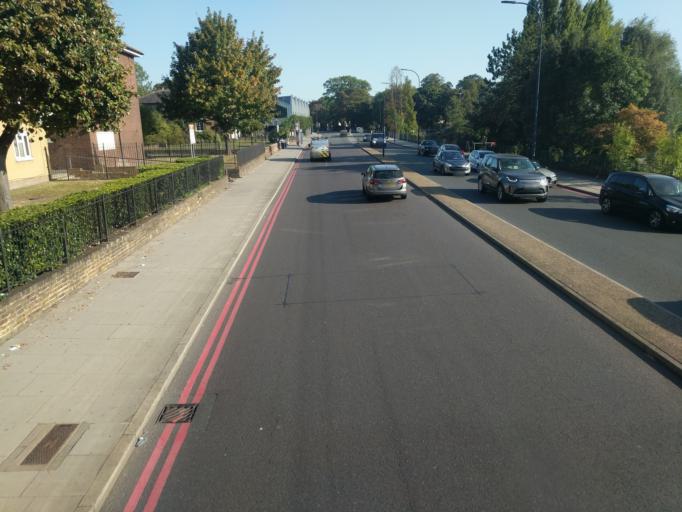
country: GB
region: England
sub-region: Greater London
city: Catford
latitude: 51.4285
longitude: -0.0127
